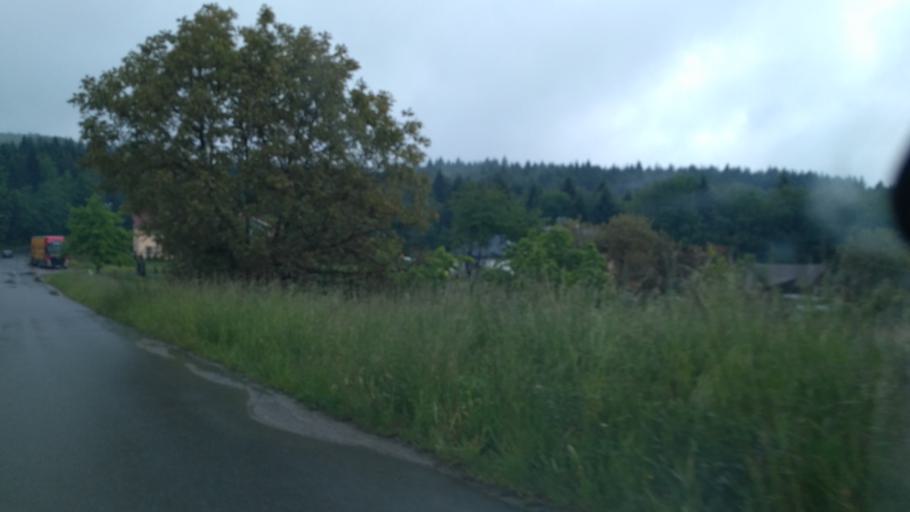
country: PL
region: Subcarpathian Voivodeship
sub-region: Powiat jasielski
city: Jaslo
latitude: 49.7690
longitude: 21.4883
